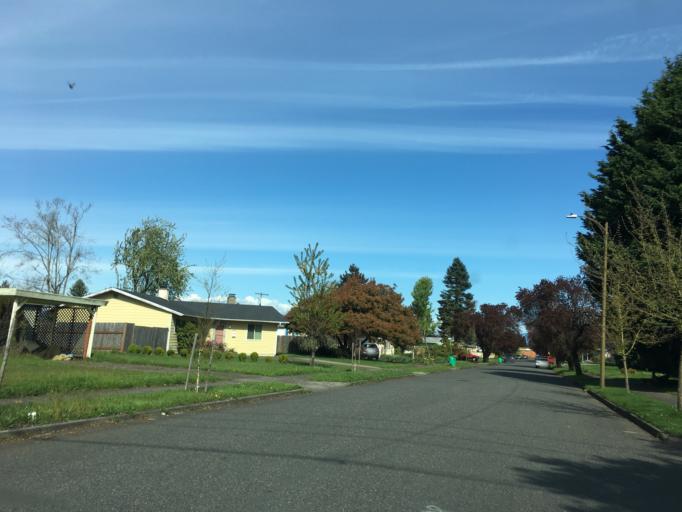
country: US
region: Oregon
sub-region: Multnomah County
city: Lents
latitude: 45.5412
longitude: -122.5373
